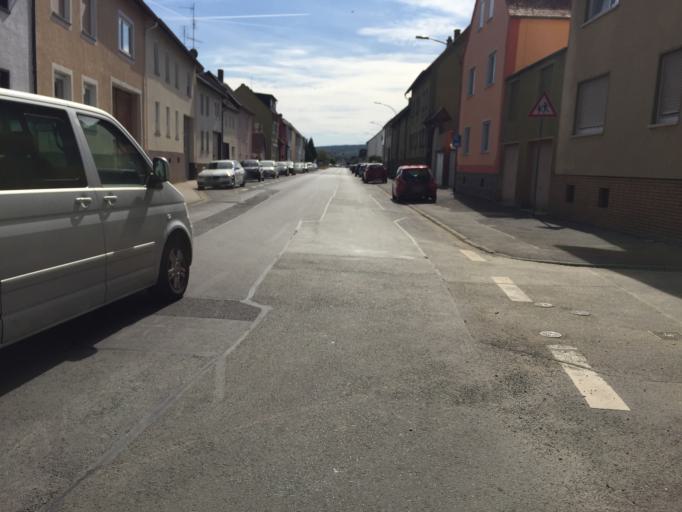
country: DE
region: Hesse
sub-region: Regierungsbezirk Giessen
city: Langgons
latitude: 50.4692
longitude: 8.6527
